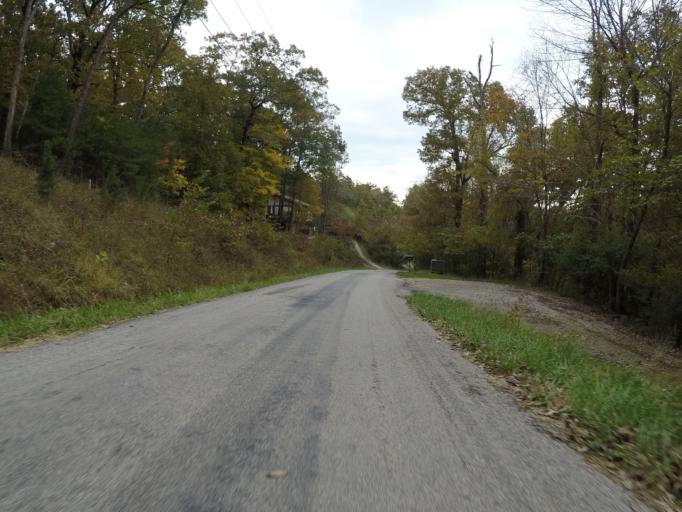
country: US
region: West Virginia
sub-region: Wayne County
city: Lavalette
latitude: 38.3597
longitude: -82.4209
